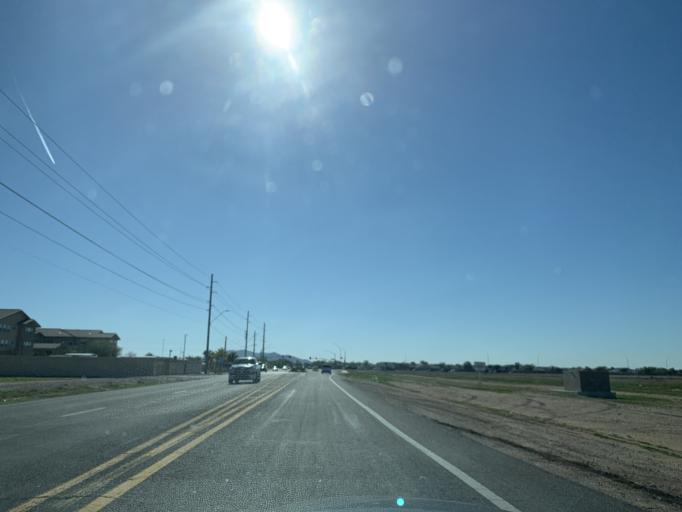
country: US
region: Arizona
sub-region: Pinal County
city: Casa Grande
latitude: 32.8971
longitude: -111.7226
